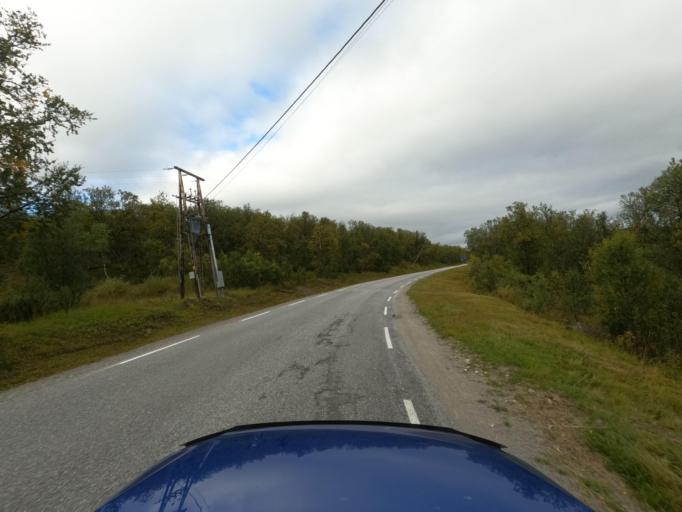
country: NO
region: Finnmark Fylke
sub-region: Porsanger
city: Lakselv
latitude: 70.2998
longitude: 25.0651
